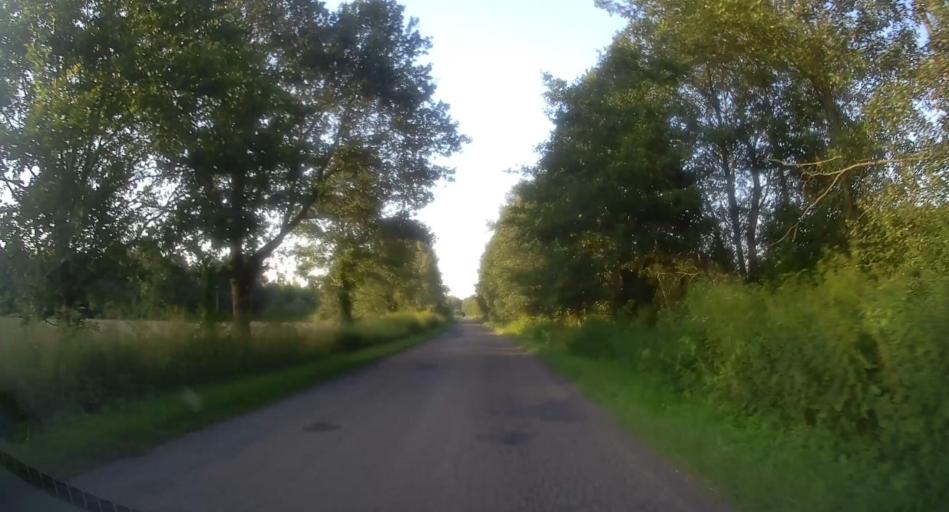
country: PL
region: Lodz Voivodeship
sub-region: Powiat skierniewicki
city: Kaweczyn Nowy
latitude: 51.8920
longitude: 20.2946
